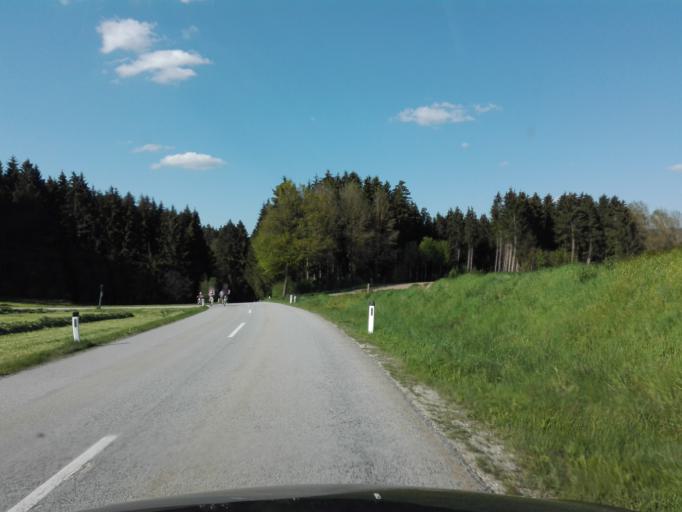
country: DE
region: Bavaria
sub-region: Lower Bavaria
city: Obernzell
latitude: 48.5039
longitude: 13.6076
